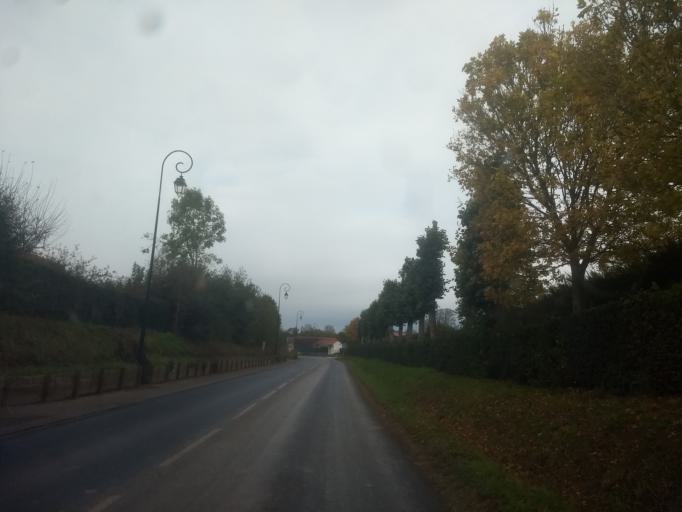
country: FR
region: Nord-Pas-de-Calais
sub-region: Departement du Pas-de-Calais
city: Wissant
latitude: 50.8808
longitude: 1.7183
